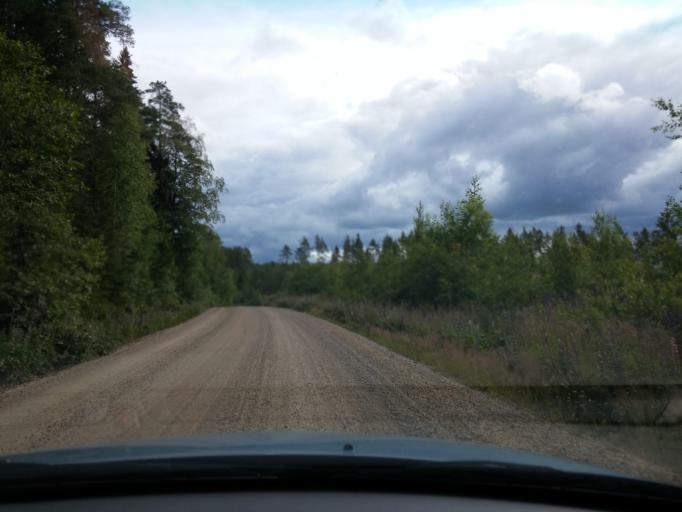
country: FI
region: Central Finland
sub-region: AEaenekoski
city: AEaenekoski
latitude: 62.7663
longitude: 25.5523
